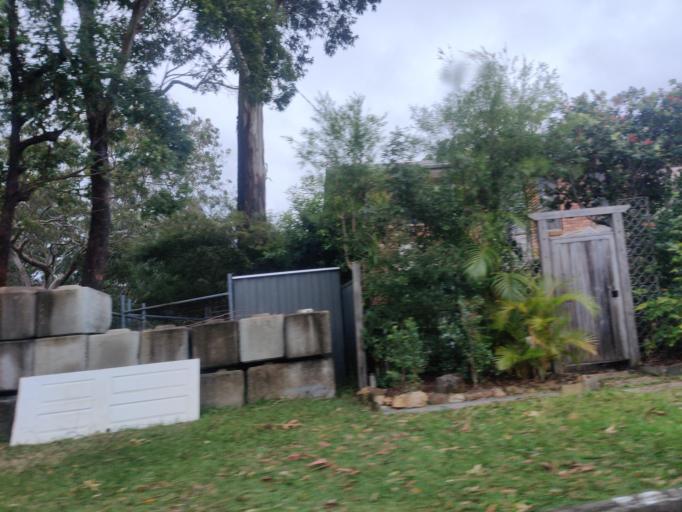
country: AU
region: New South Wales
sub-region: Great Lakes
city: Forster
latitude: -32.3773
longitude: 152.5029
